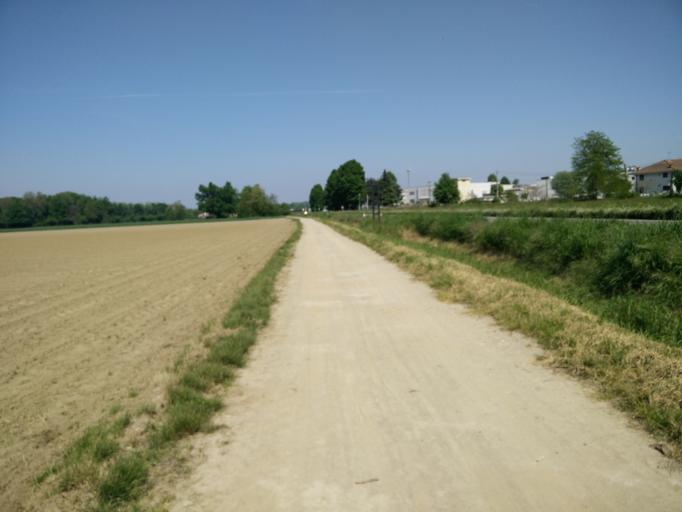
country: IT
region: Piedmont
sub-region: Provincia di Torino
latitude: 44.9571
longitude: 7.5615
